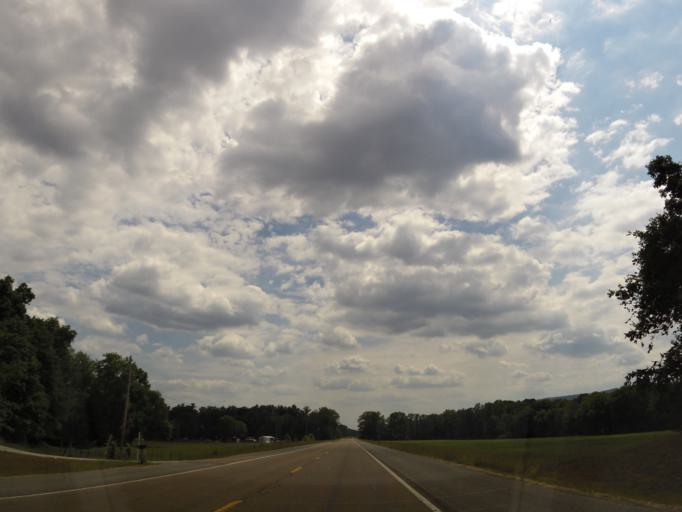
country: US
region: Tennessee
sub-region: Marion County
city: Powells Crossroads
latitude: 35.2728
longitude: -85.4597
